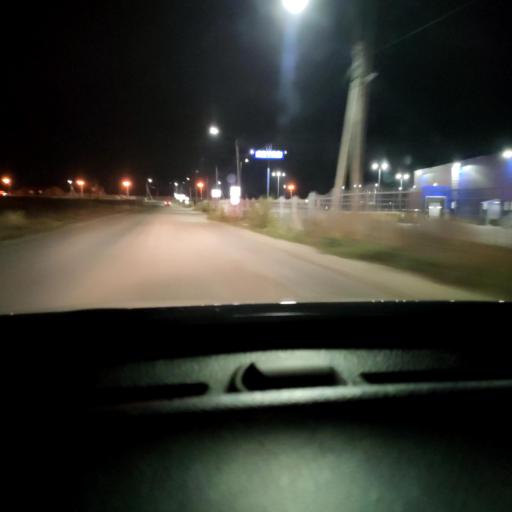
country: RU
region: Voronezj
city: Pridonskoy
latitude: 51.6541
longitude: 39.0634
